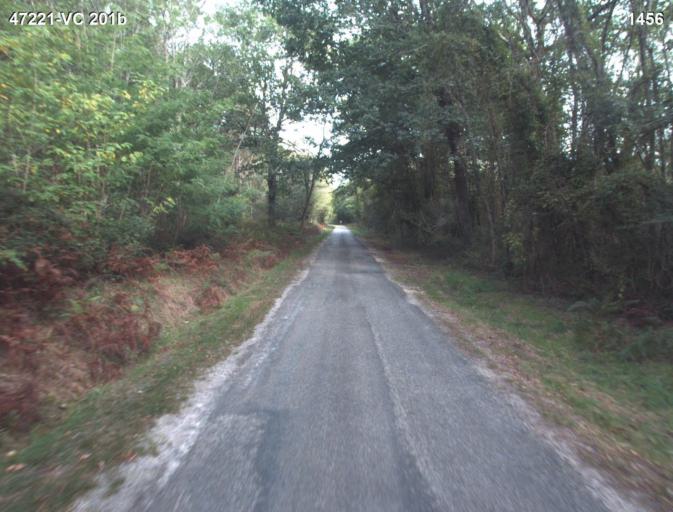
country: FR
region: Aquitaine
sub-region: Departement du Lot-et-Garonne
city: Mezin
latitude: 44.0811
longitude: 0.2324
